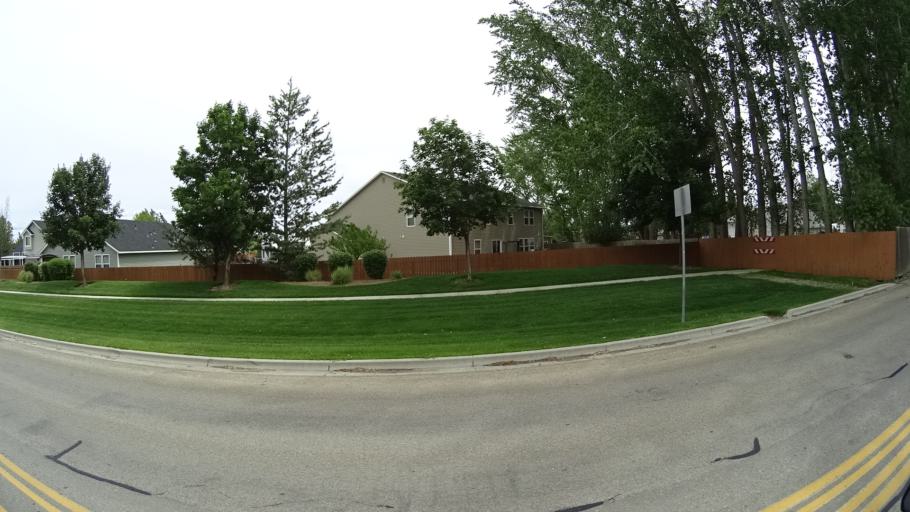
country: US
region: Idaho
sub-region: Ada County
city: Meridian
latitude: 43.5624
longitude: -116.3745
